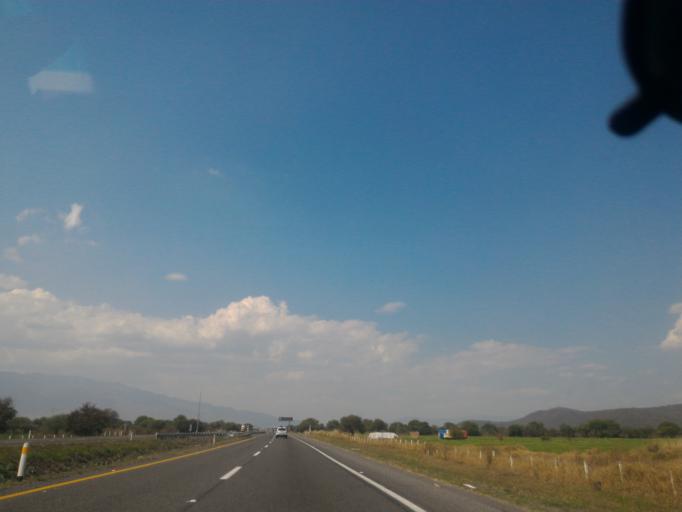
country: MX
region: Jalisco
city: Usmajac
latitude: 19.9163
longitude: -103.5274
